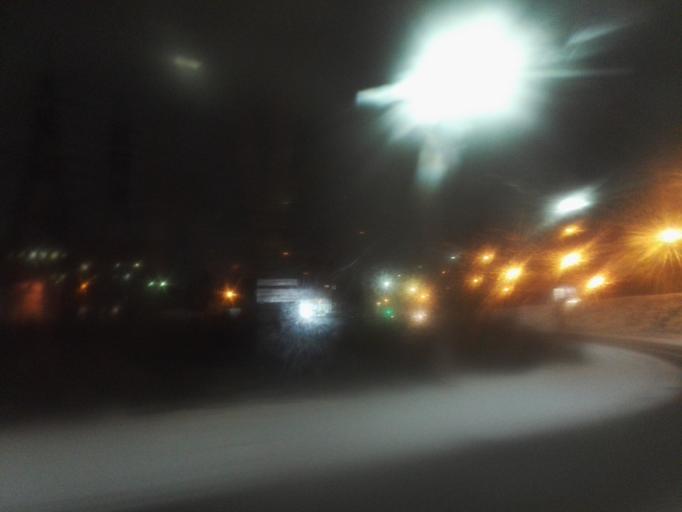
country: RU
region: Tula
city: Tula
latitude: 54.1715
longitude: 37.6364
